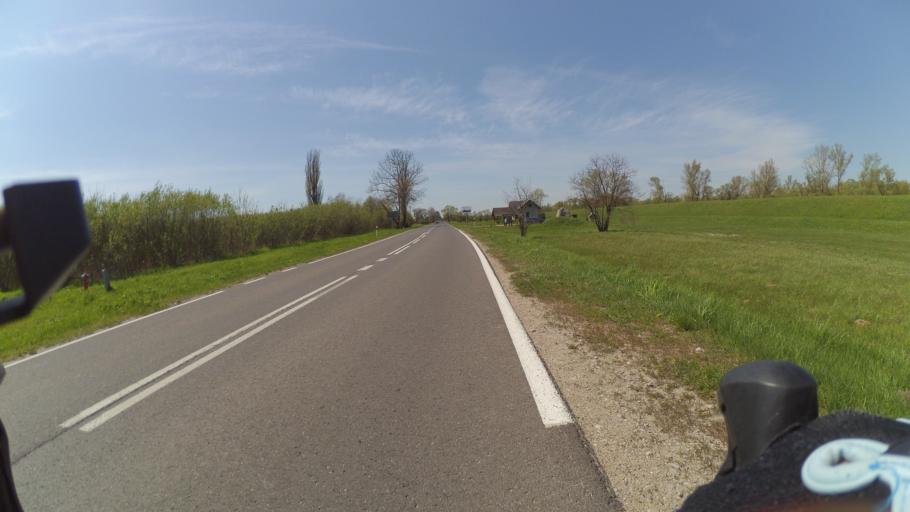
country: PL
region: Masovian Voivodeship
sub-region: Powiat plonski
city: Czerwinsk Nad Wisla
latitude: 52.3773
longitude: 20.3519
